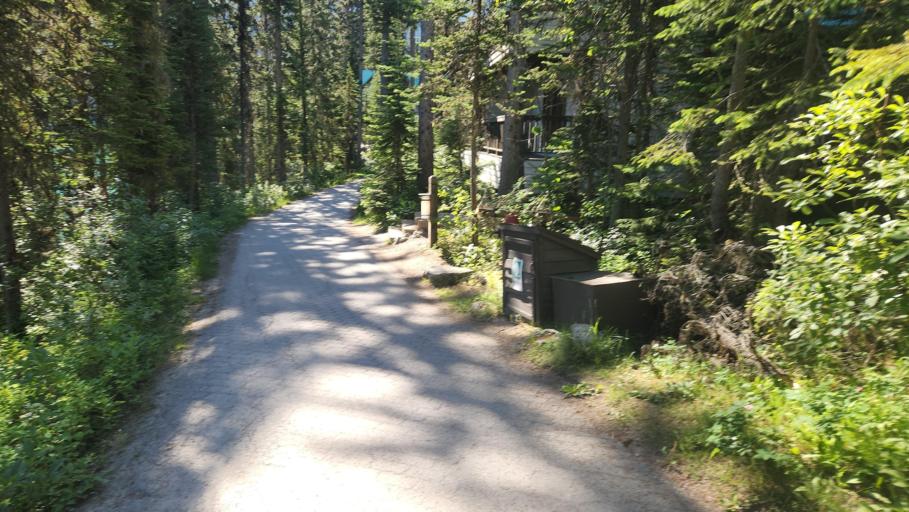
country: CA
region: Alberta
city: Lake Louise
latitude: 51.4391
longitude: -116.5357
